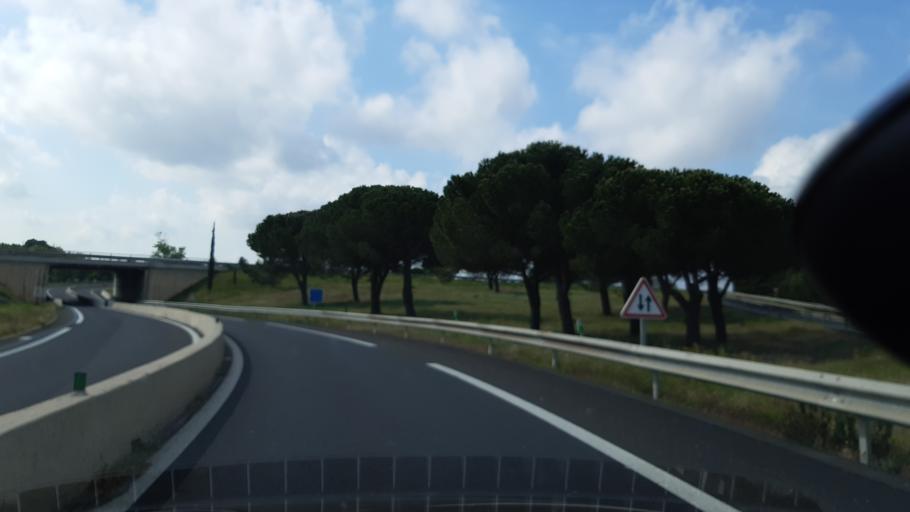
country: FR
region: Languedoc-Roussillon
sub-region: Departement de l'Aude
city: Narbonne
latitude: 43.1774
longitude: 3.0339
